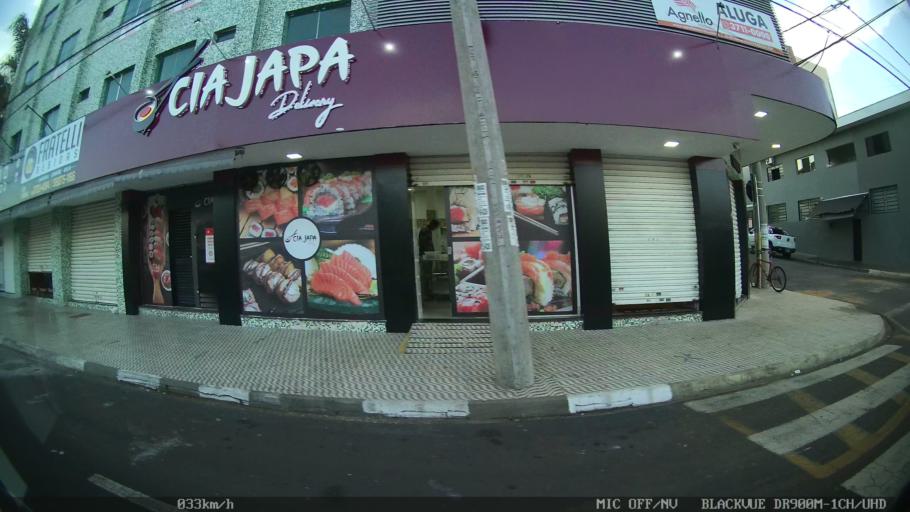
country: BR
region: Sao Paulo
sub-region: Franca
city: Franca
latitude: -20.5281
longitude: -47.4028
